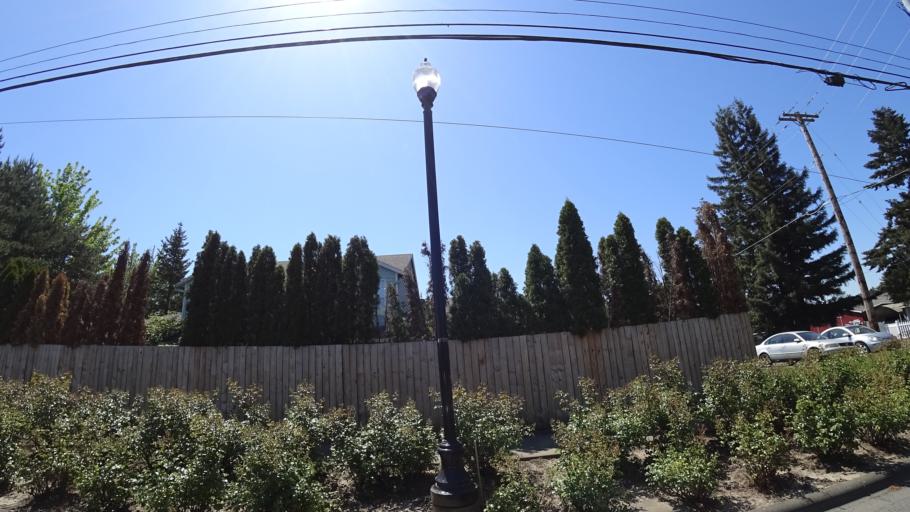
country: US
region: Oregon
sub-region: Washington County
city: Aloha
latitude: 45.5151
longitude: -122.8886
